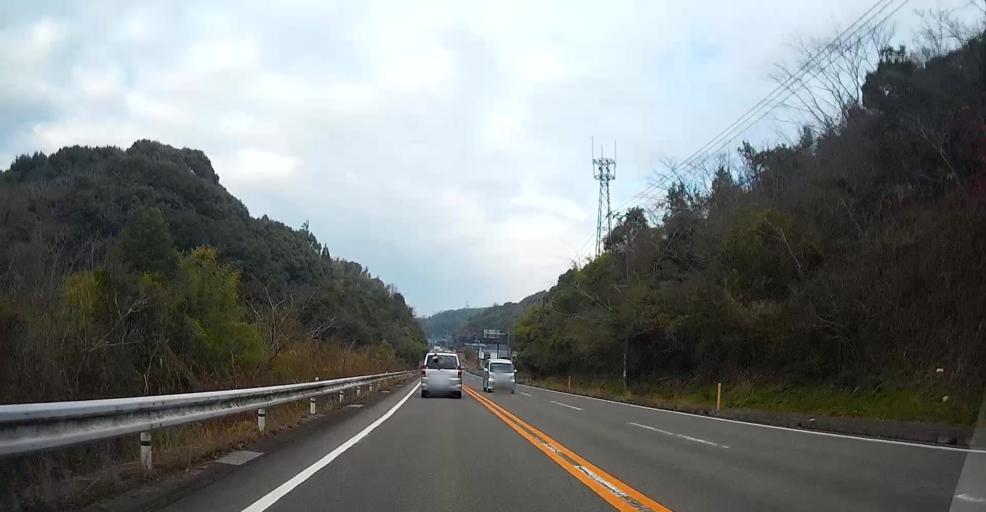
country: JP
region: Kumamoto
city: Yatsushiro
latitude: 32.5600
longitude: 130.4144
